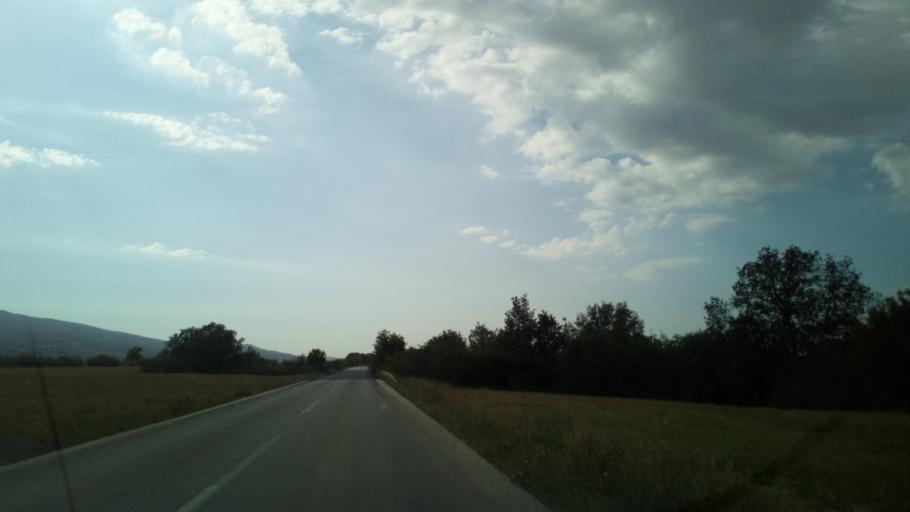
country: GR
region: Central Macedonia
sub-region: Nomos Thessalonikis
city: Gerakarou
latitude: 40.5946
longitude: 23.2325
